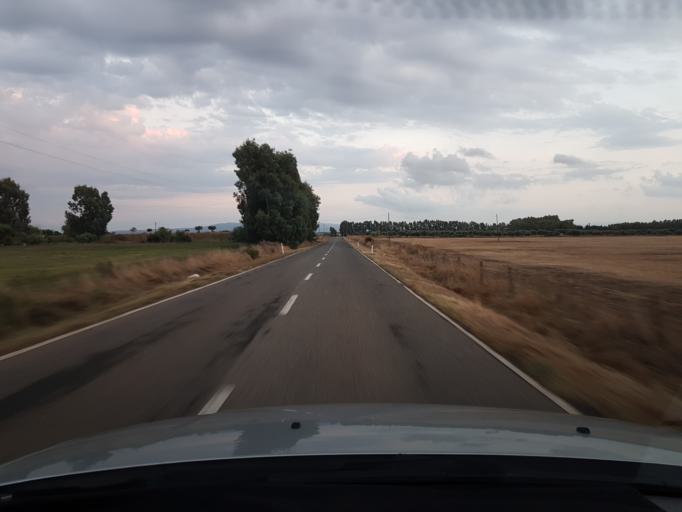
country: IT
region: Sardinia
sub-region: Provincia di Oristano
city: Milis
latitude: 40.0266
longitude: 8.6407
